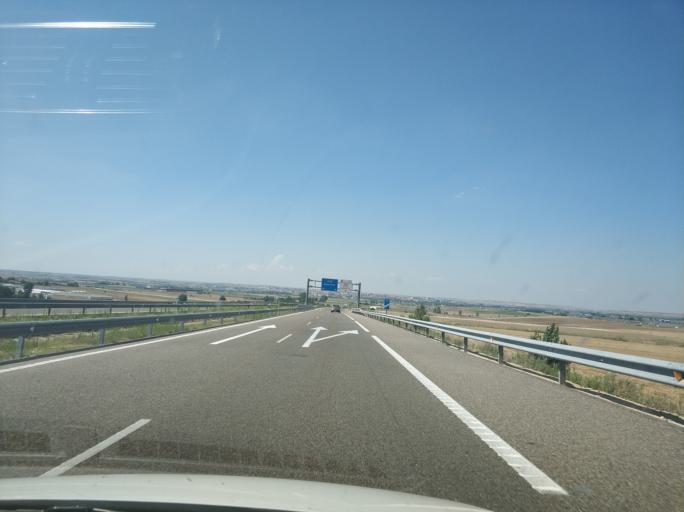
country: ES
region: Castille and Leon
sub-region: Provincia de Zamora
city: Morales del Vino
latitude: 41.4479
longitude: -5.7192
